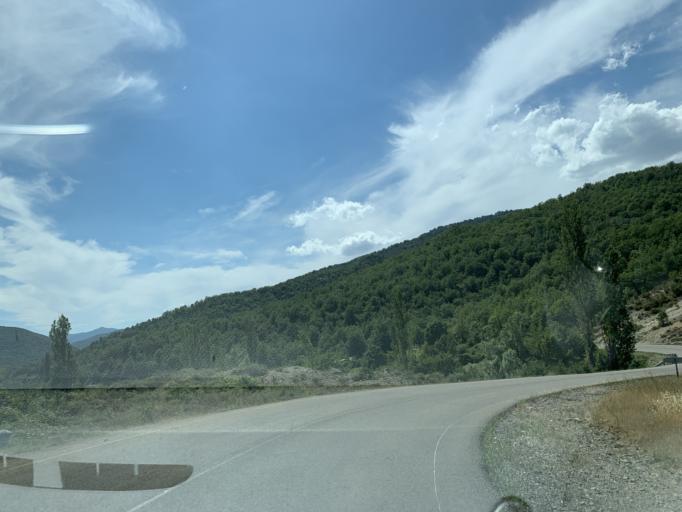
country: ES
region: Aragon
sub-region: Provincia de Huesca
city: Jasa
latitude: 42.6454
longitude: -0.6424
